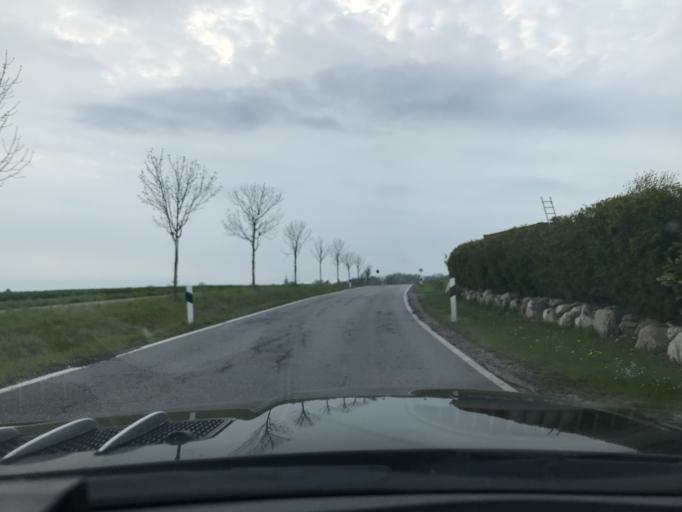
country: DE
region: Schleswig-Holstein
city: Burg auf Fehmarn
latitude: 54.4303
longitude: 11.2212
